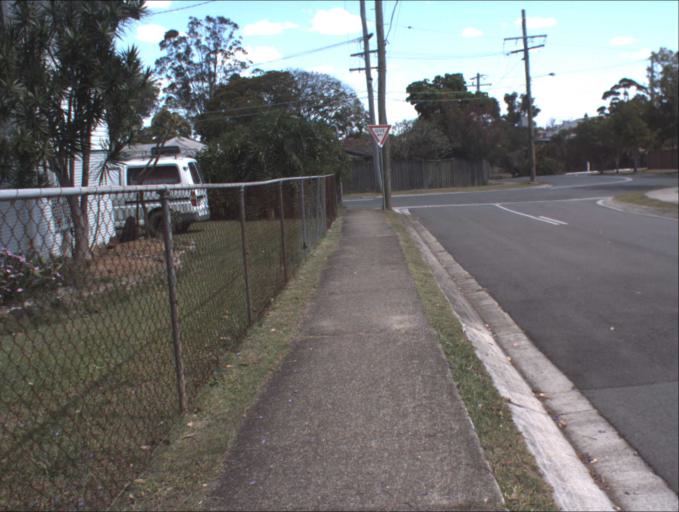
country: AU
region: Queensland
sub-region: Logan
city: Rochedale South
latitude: -27.5972
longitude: 153.1111
